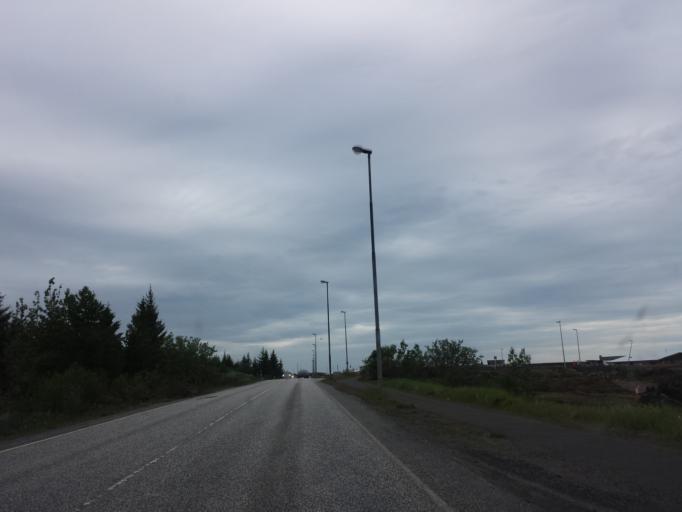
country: IS
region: Capital Region
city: Hafnarfjoerdur
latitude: 64.0848
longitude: -21.9552
